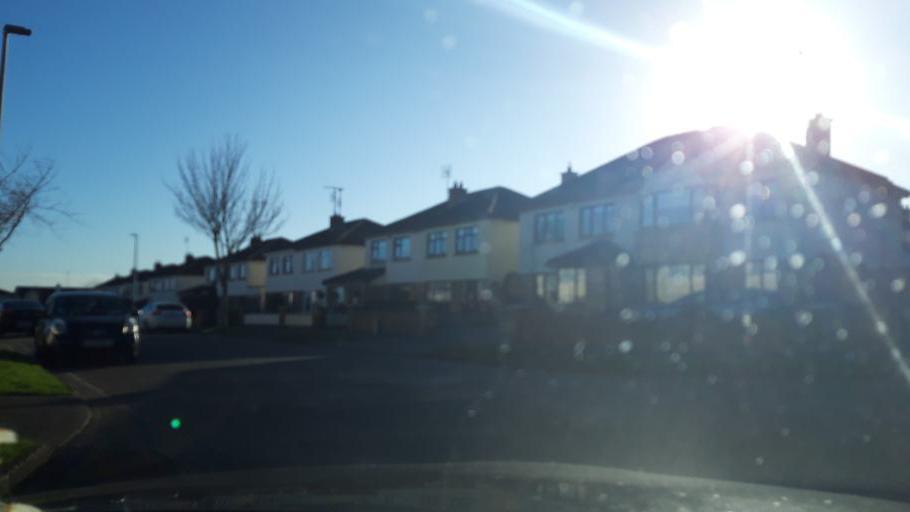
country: IE
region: Leinster
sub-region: Fingal County
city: Swords
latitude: 53.4528
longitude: -6.2490
